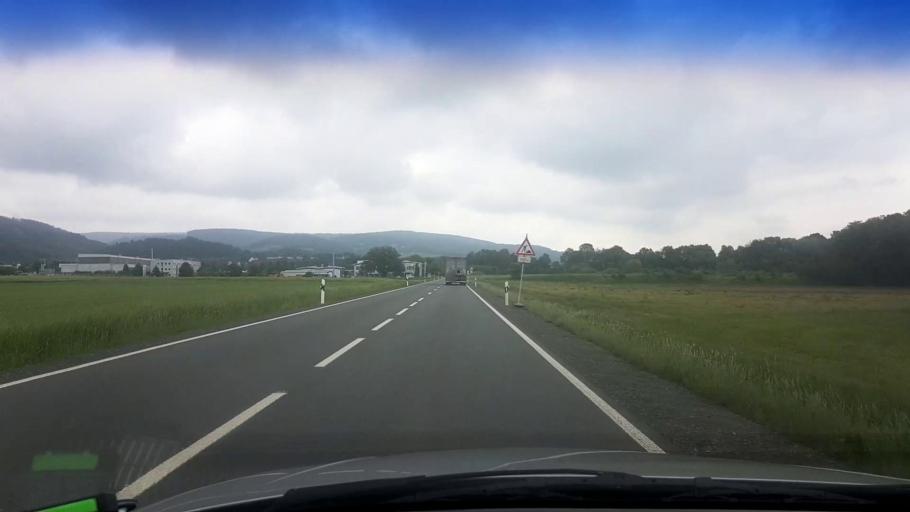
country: DE
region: Bavaria
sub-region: Upper Franconia
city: Gesees
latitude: 50.0156
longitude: 11.6674
